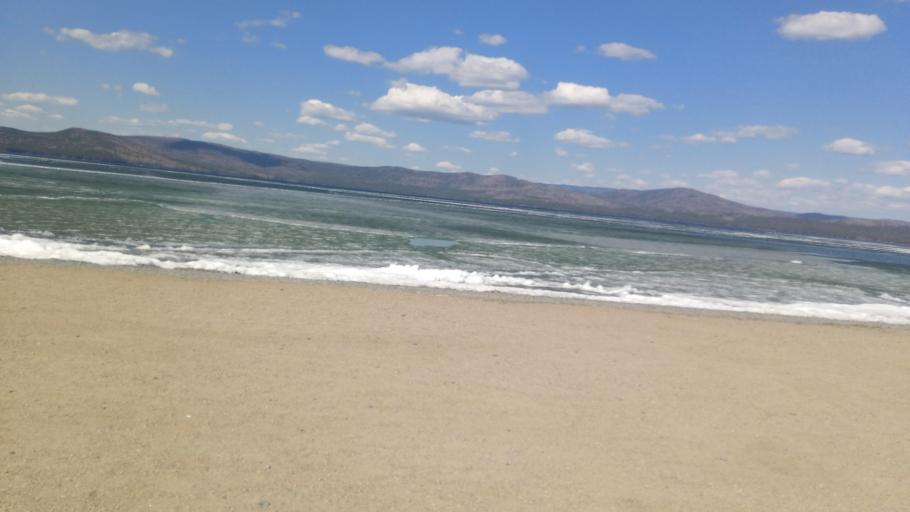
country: RU
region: Chelyabinsk
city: Turgoyak
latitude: 55.1529
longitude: 60.1099
